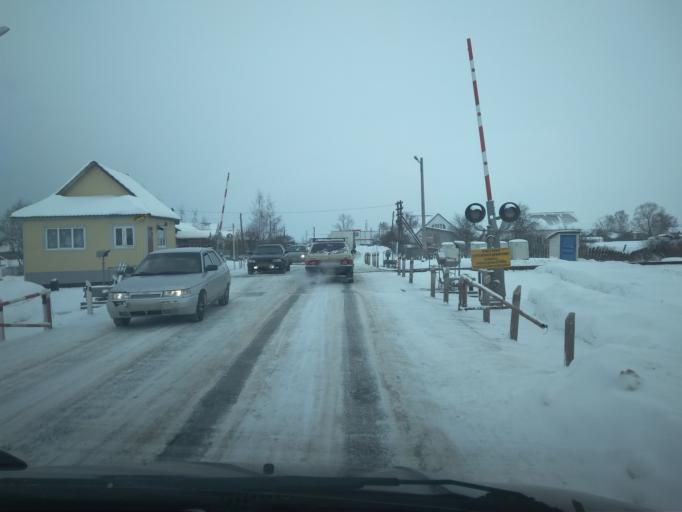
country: RU
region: Mordoviya
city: Kemlya
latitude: 54.6897
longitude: 45.2759
